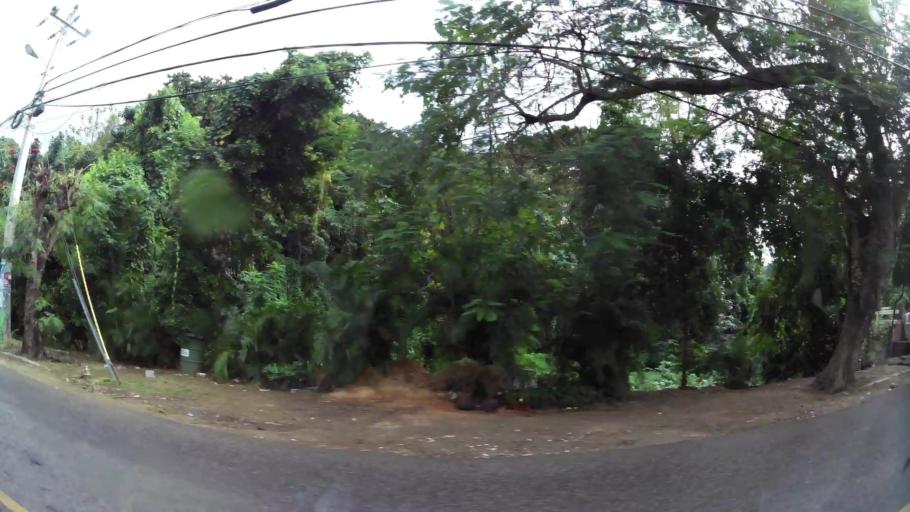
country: DO
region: Nacional
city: La Agustina
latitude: 18.5081
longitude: -69.9474
